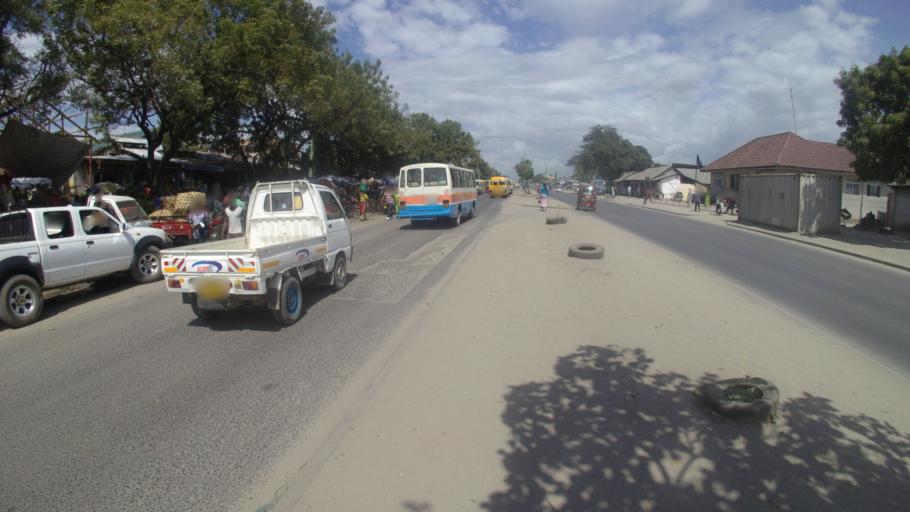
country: TZ
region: Dar es Salaam
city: Dar es Salaam
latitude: -6.8348
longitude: 39.2465
